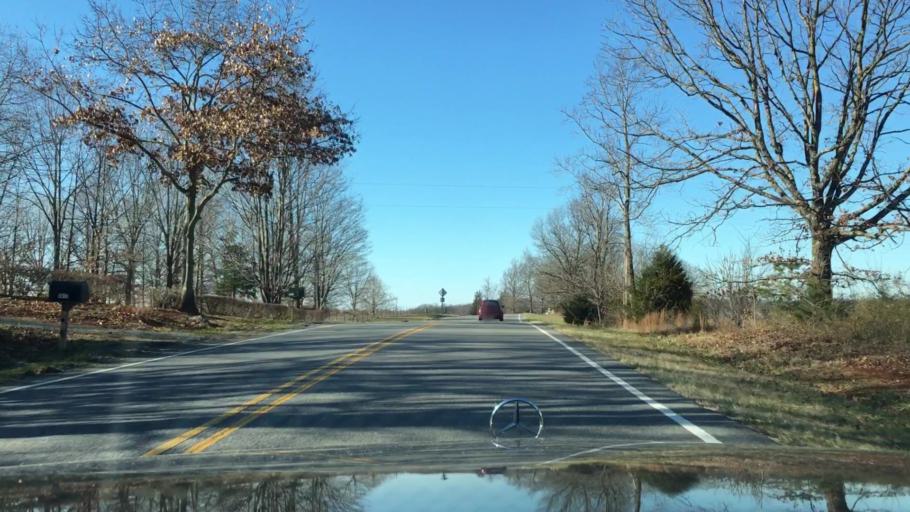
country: US
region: Virginia
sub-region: City of Bedford
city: Bedford
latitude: 37.2194
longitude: -79.4814
